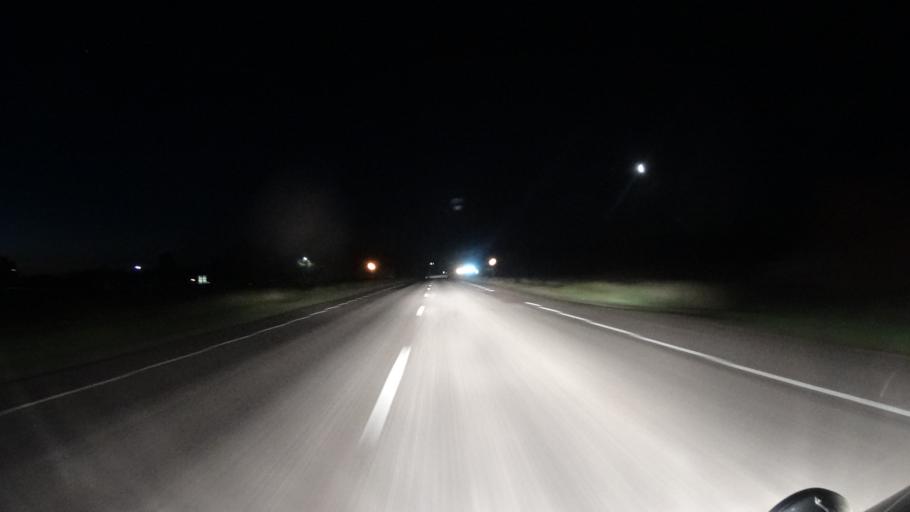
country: SE
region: OEstergoetland
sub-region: Vadstena Kommun
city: Herrestad
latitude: 58.3029
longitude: 14.8276
